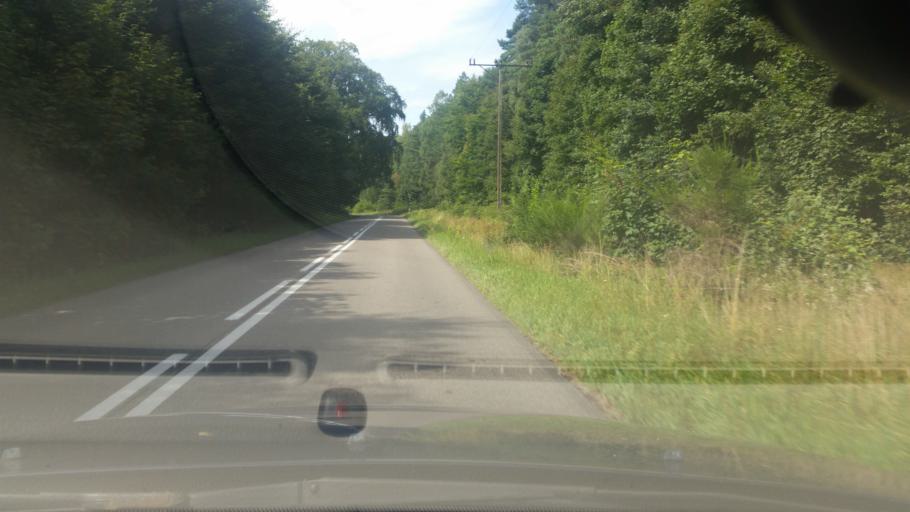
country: PL
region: Pomeranian Voivodeship
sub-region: Powiat wejherowski
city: Choczewo
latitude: 54.7473
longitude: 17.7302
